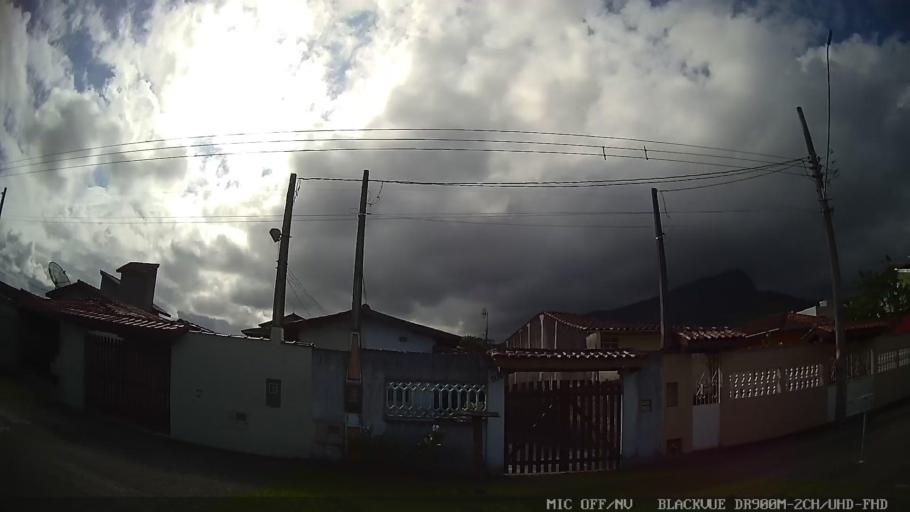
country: BR
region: Sao Paulo
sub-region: Caraguatatuba
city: Caraguatatuba
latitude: -23.6360
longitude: -45.4393
